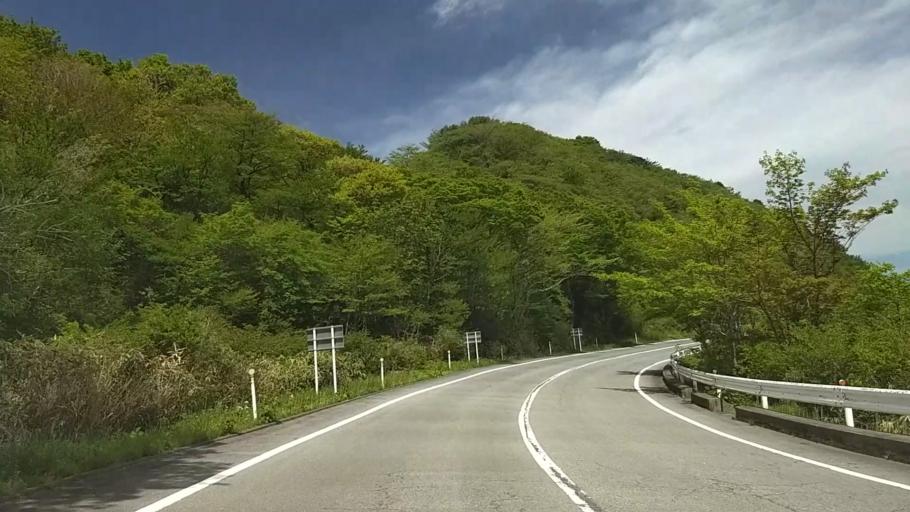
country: JP
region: Kanagawa
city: Hakone
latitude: 35.1950
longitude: 139.0661
